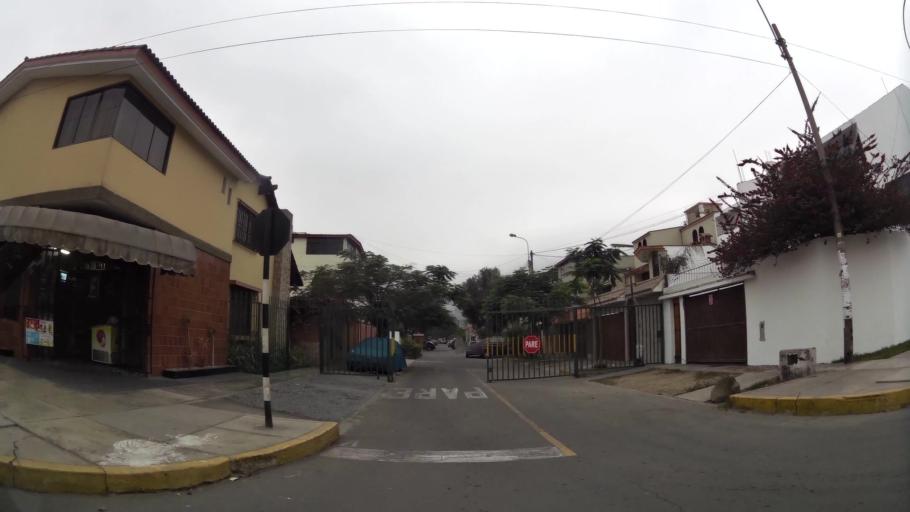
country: PE
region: Lima
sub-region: Lima
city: La Molina
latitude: -12.0992
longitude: -76.9499
